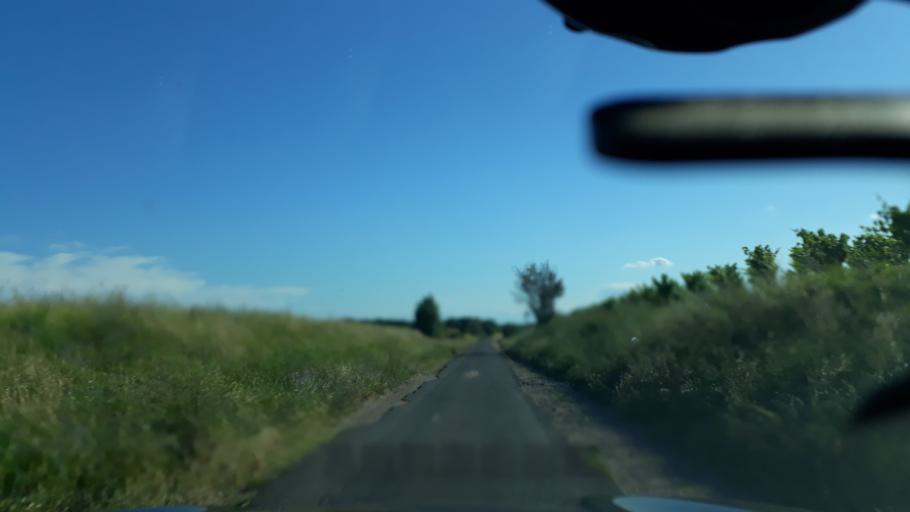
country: FR
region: Languedoc-Roussillon
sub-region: Departement de l'Herault
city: Marseillan
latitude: 43.3412
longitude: 3.5097
